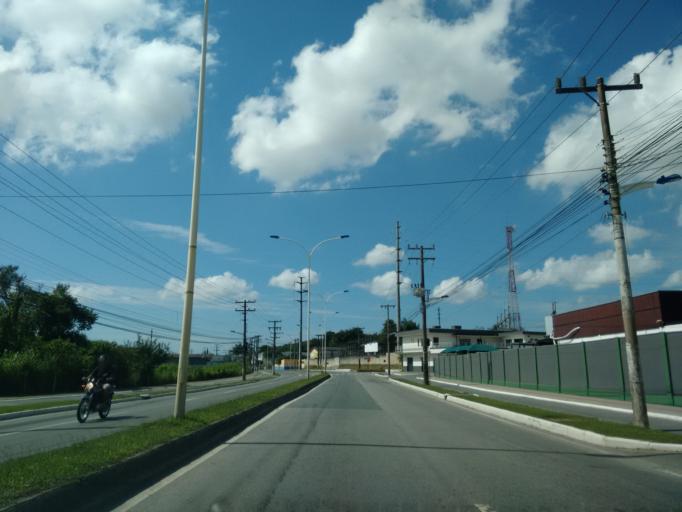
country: BR
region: Santa Catarina
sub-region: Itajai
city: Itajai
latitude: -26.8913
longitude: -48.7167
